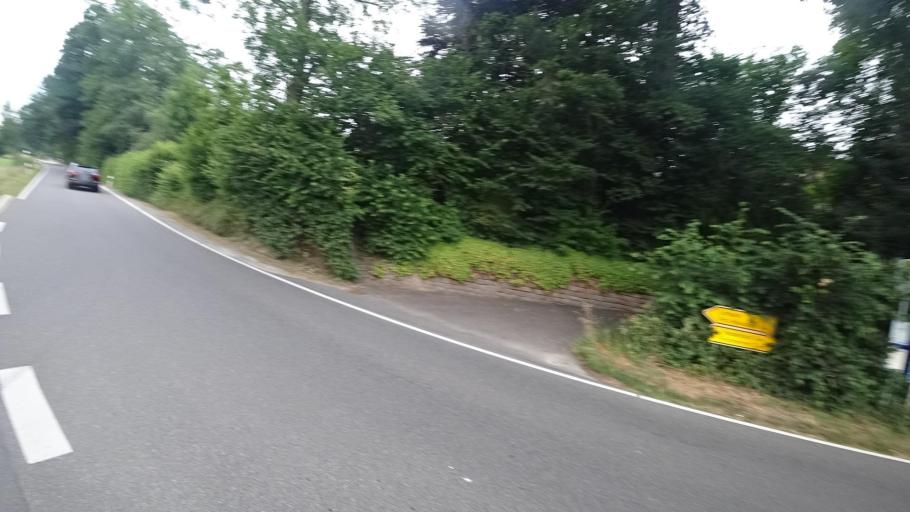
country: DE
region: Rheinland-Pfalz
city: Seifen
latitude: 50.6882
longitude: 7.5162
